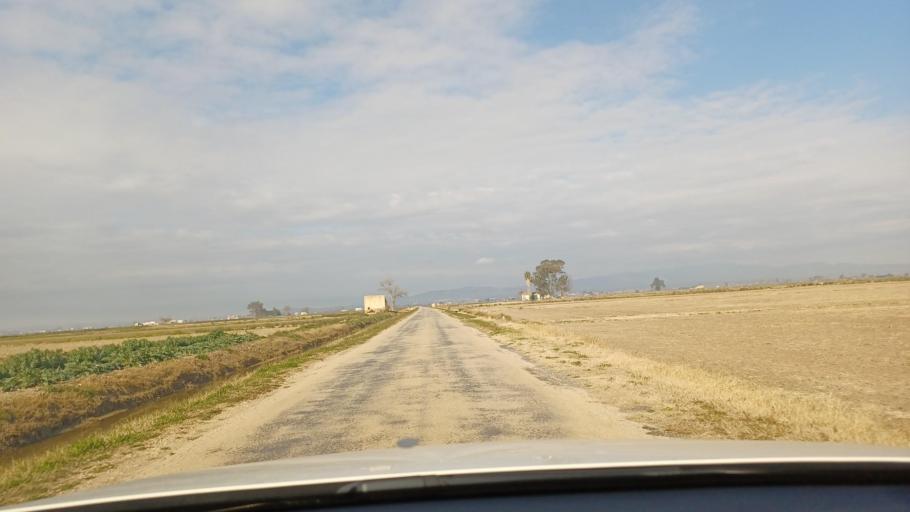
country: ES
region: Catalonia
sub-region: Provincia de Tarragona
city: Deltebre
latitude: 40.6844
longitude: 0.6553
